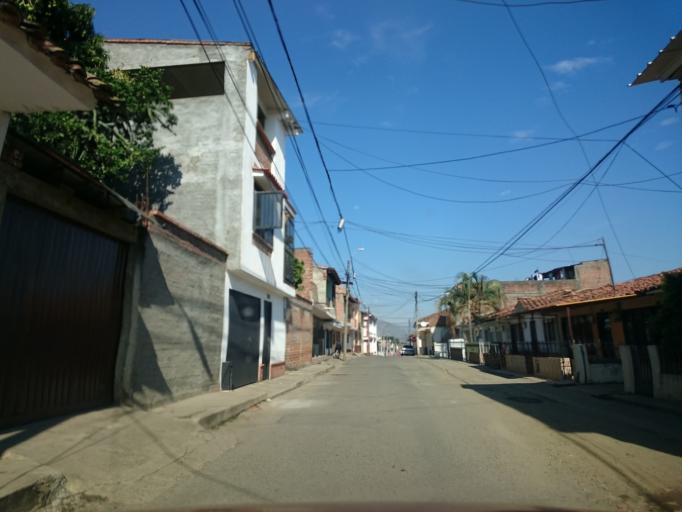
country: CO
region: Cauca
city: Santander de Quilichao
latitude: 3.0115
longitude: -76.4816
